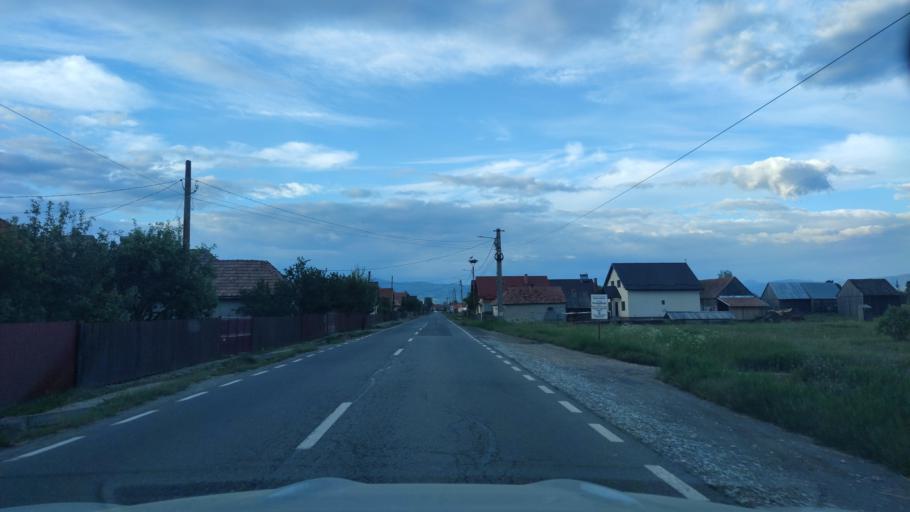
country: RO
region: Harghita
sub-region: Comuna Joseni
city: Joseni
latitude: 46.6993
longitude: 25.4854
